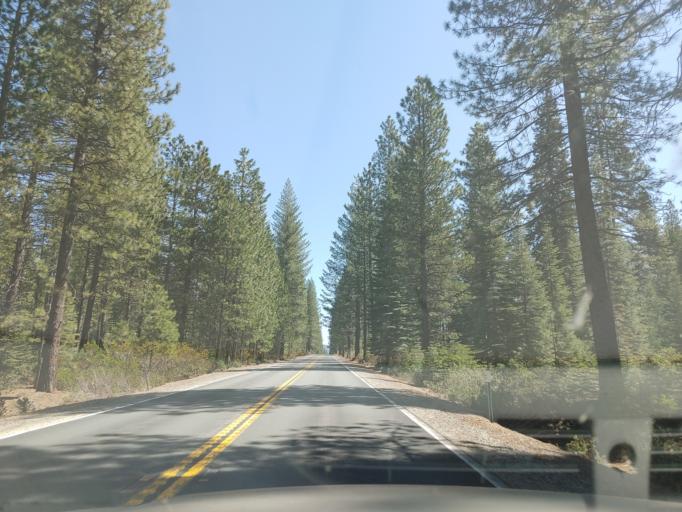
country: US
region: California
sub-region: Siskiyou County
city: McCloud
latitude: 41.2664
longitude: -121.8746
